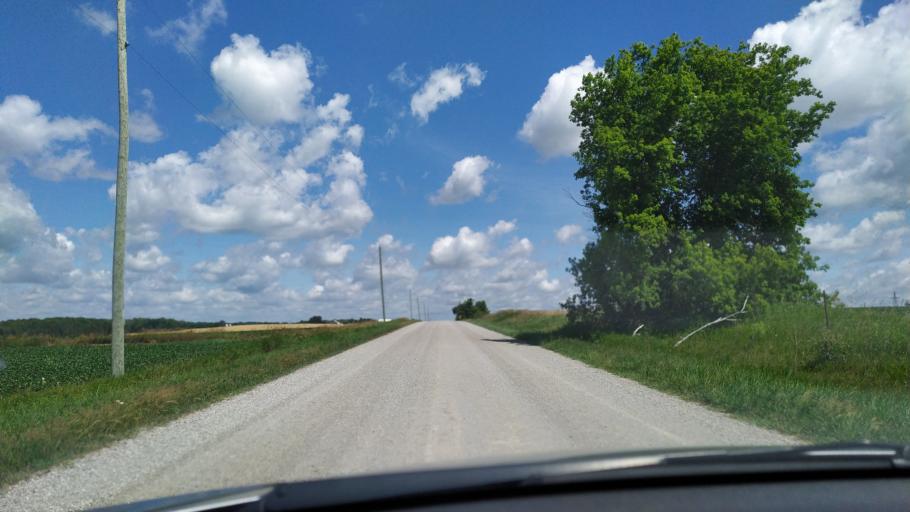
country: CA
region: Ontario
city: Stratford
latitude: 43.3831
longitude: -80.7619
